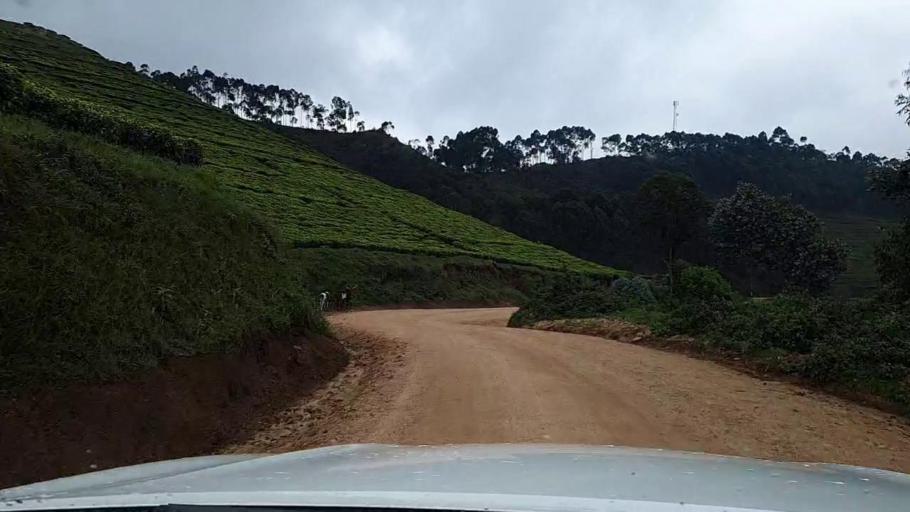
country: RW
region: Western Province
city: Kibuye
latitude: -2.2939
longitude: 29.3828
